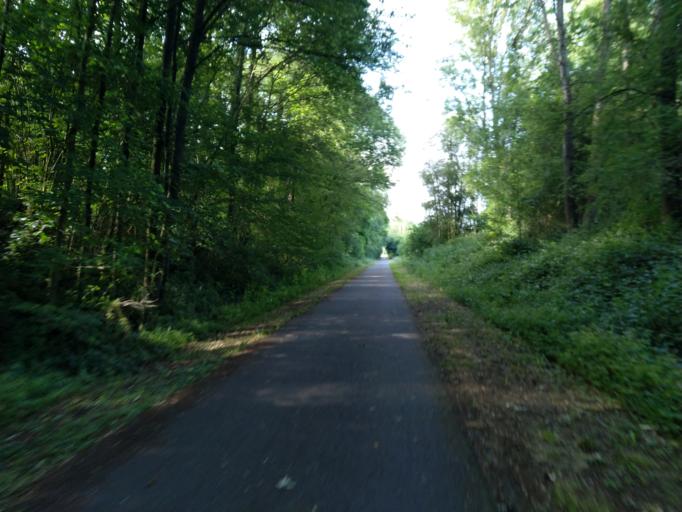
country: BE
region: Wallonia
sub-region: Province du Hainaut
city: Erquelinnes
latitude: 50.3294
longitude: 4.0987
